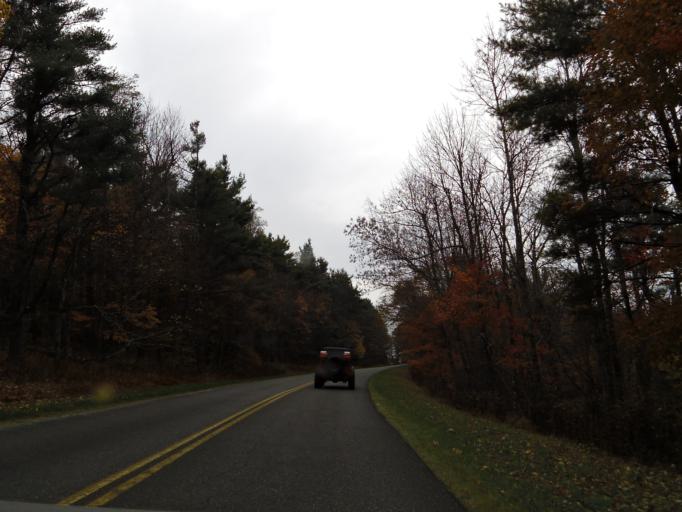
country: US
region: North Carolina
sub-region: Ashe County
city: West Jefferson
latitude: 36.2440
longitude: -81.4771
